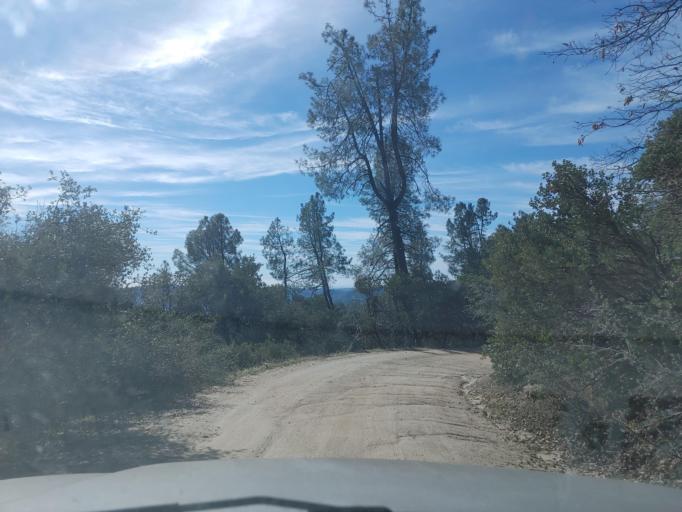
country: US
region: California
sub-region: Madera County
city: Ahwahnee
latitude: 37.4155
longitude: -119.6959
